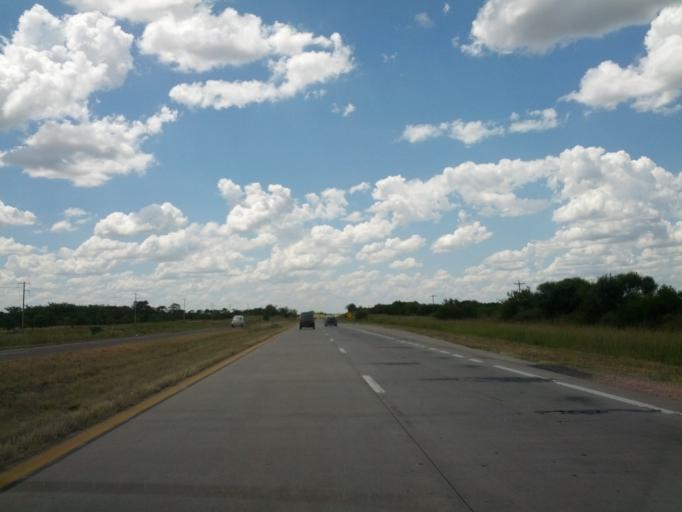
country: AR
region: Entre Rios
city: Gualeguaychu
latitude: -32.9488
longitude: -58.5796
